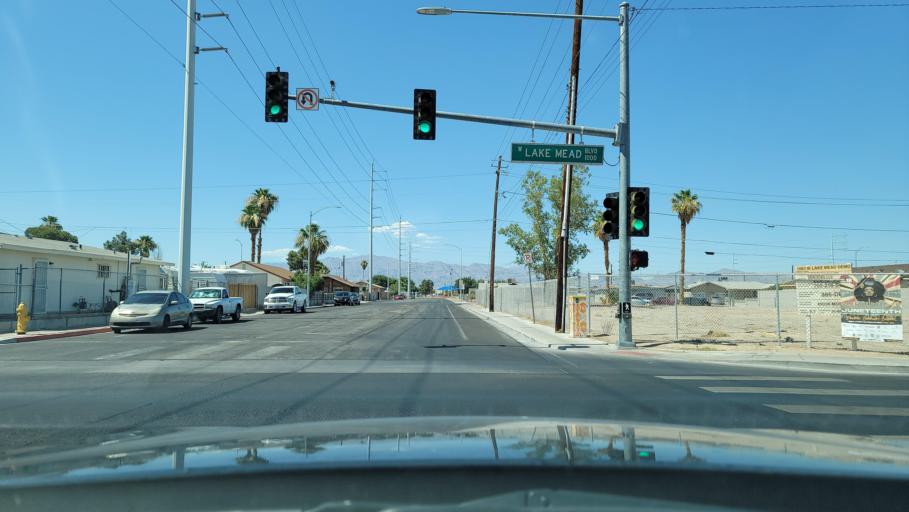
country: US
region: Nevada
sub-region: Clark County
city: Las Vegas
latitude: 36.1964
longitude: -115.1563
